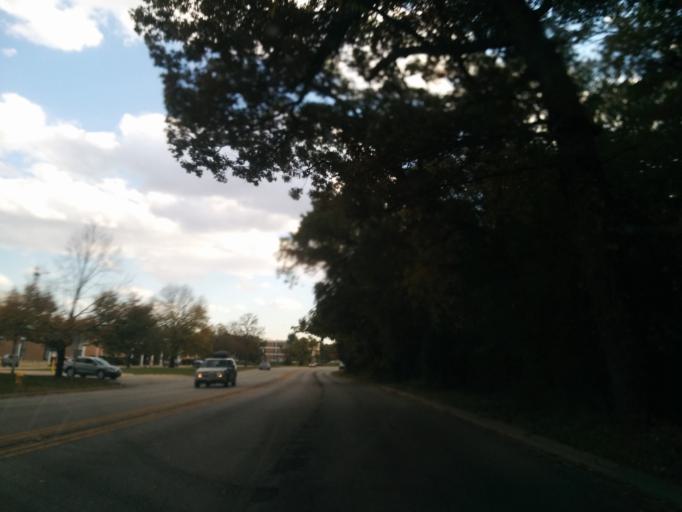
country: US
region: Illinois
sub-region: Cook County
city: Park Ridge
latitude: 42.0025
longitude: -87.8553
